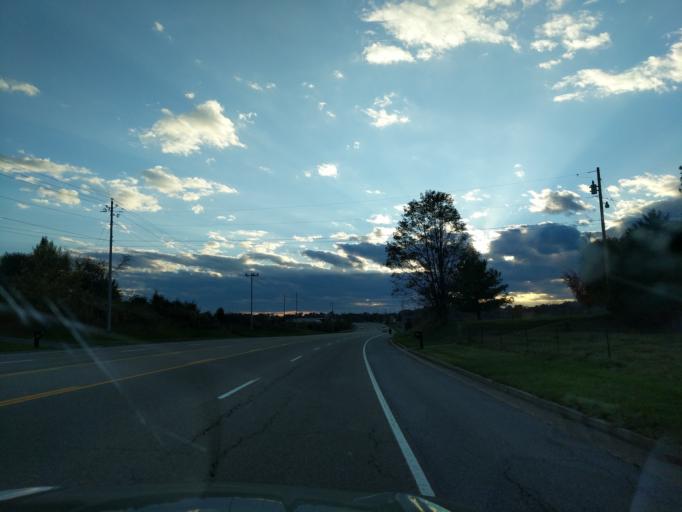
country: US
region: Tennessee
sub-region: Washington County
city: Spurgeon
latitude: 36.4262
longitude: -82.4584
